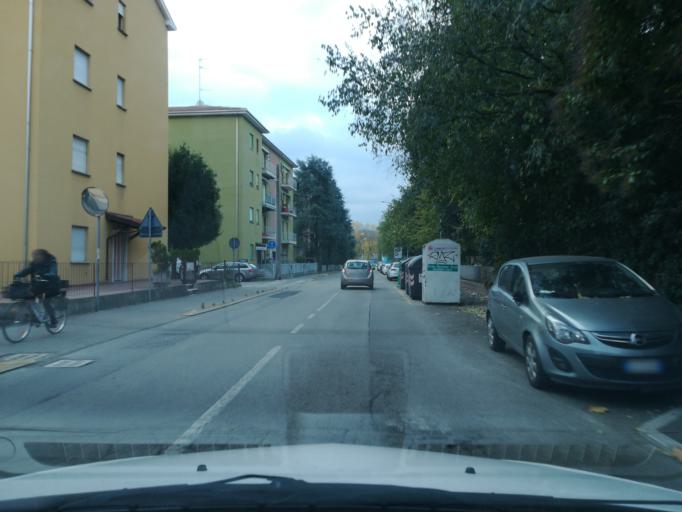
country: IT
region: Emilia-Romagna
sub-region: Provincia di Bologna
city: Imola
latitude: 44.3478
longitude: 11.7188
